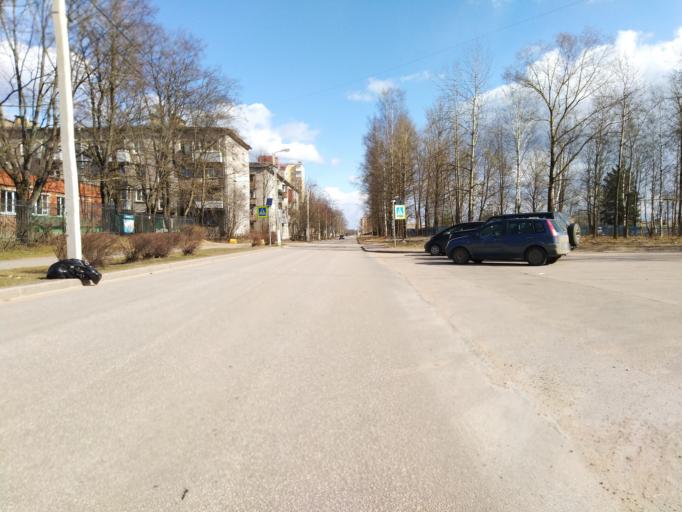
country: RU
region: Leningrad
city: Novoye Devyatkino
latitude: 60.1076
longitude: 30.4920
